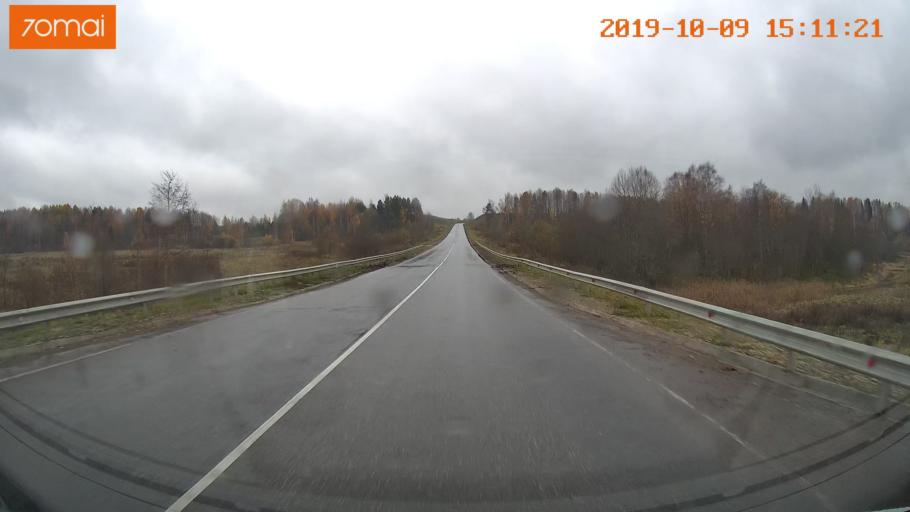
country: RU
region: Kostroma
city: Susanino
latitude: 58.1661
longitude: 41.6304
